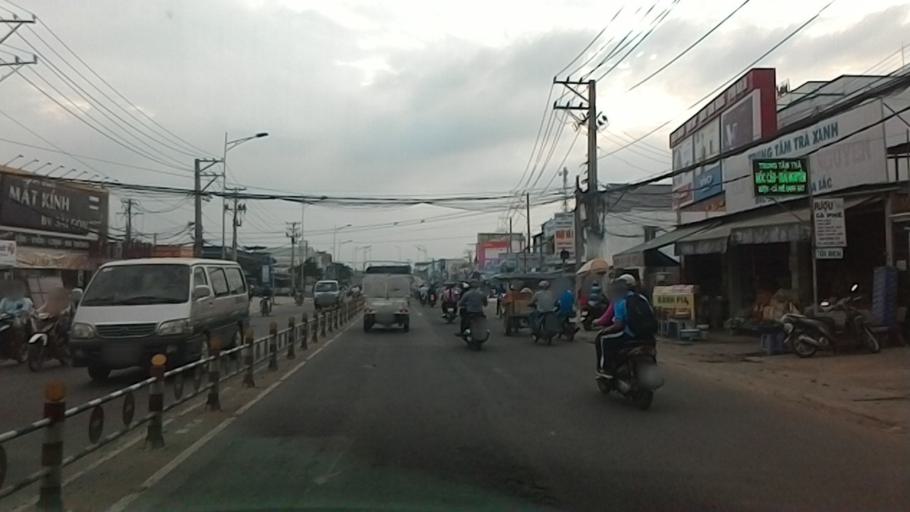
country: VN
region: Can Tho
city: Cai Rang
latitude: 10.0112
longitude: 105.7521
